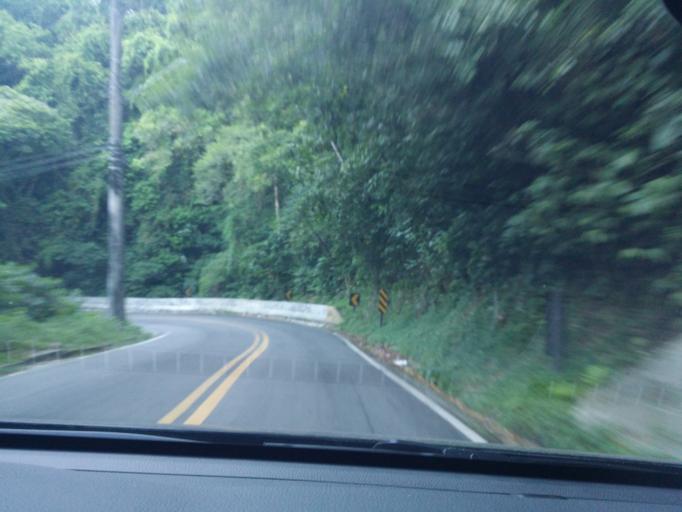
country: BR
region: Sao Paulo
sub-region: Sao Sebastiao
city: Sao Sebastiao
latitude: -23.7843
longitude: -45.5984
